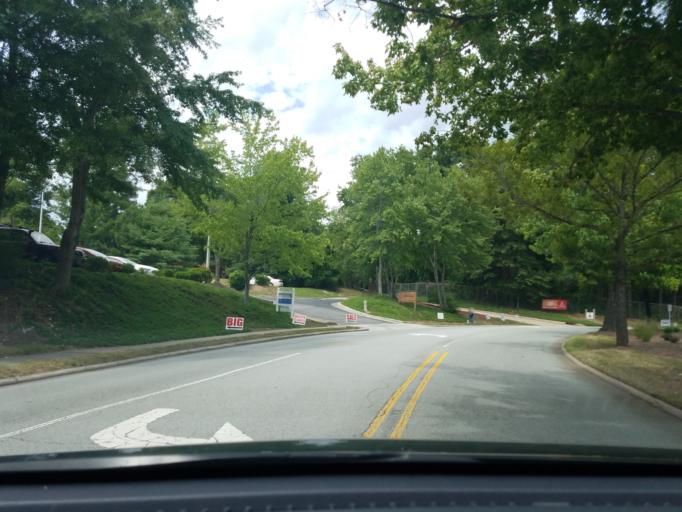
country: US
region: North Carolina
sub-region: Orange County
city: Chapel Hill
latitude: 35.9320
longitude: -79.0273
